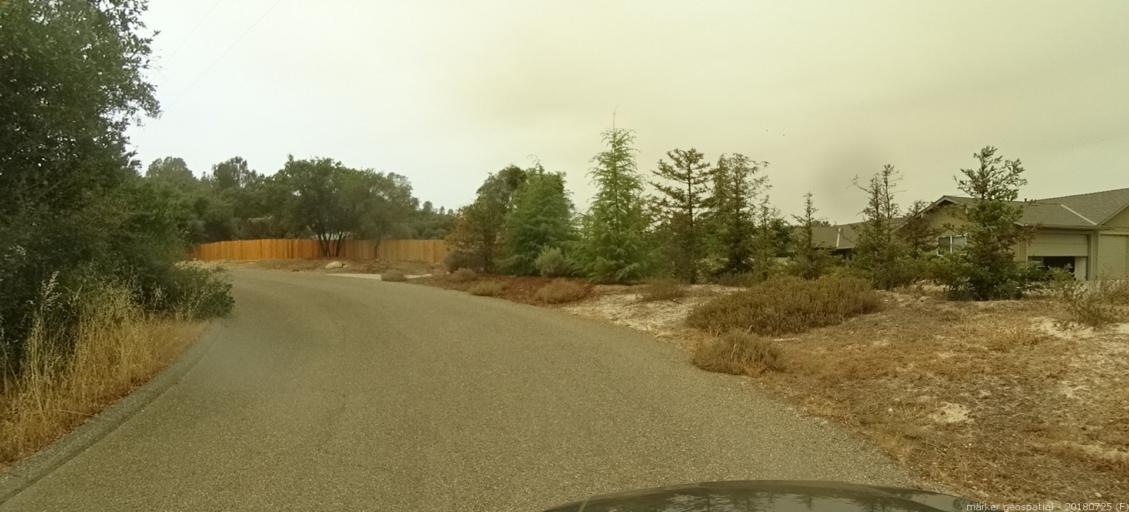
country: US
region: California
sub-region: Madera County
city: Coarsegold
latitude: 37.1866
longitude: -119.6759
